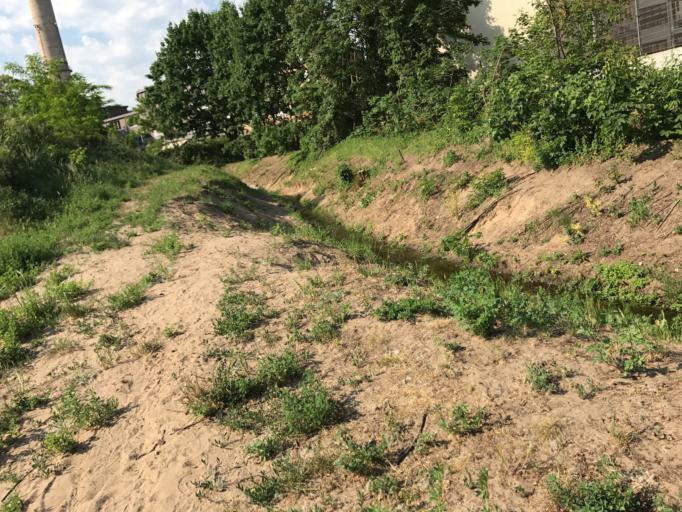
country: DE
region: Berlin
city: Tiergarten Bezirk
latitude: 52.5343
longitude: 13.3736
